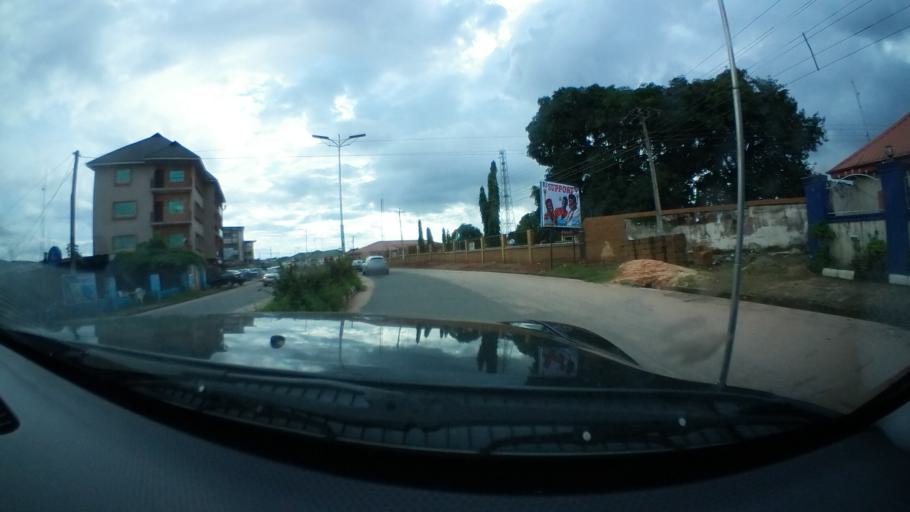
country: NG
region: Imo
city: Orlu
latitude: 5.7984
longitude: 7.0375
